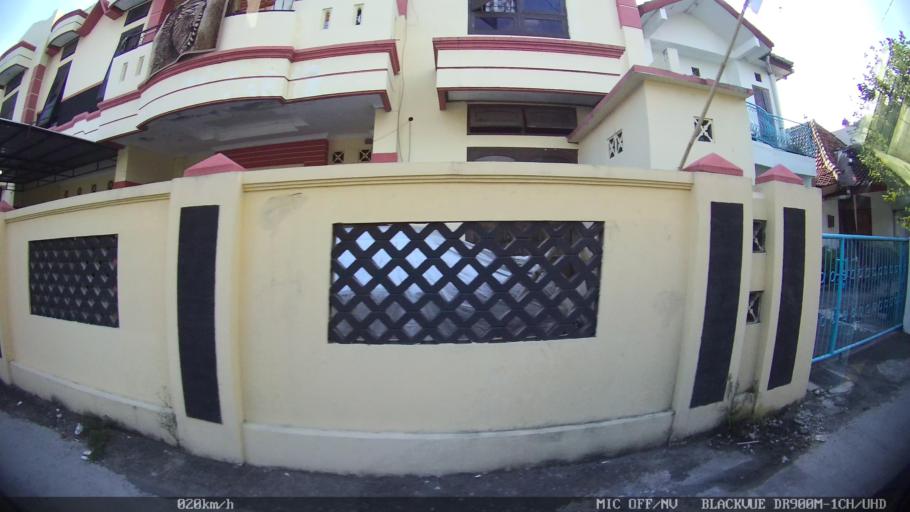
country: ID
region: Daerah Istimewa Yogyakarta
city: Yogyakarta
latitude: -7.8183
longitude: 110.3814
